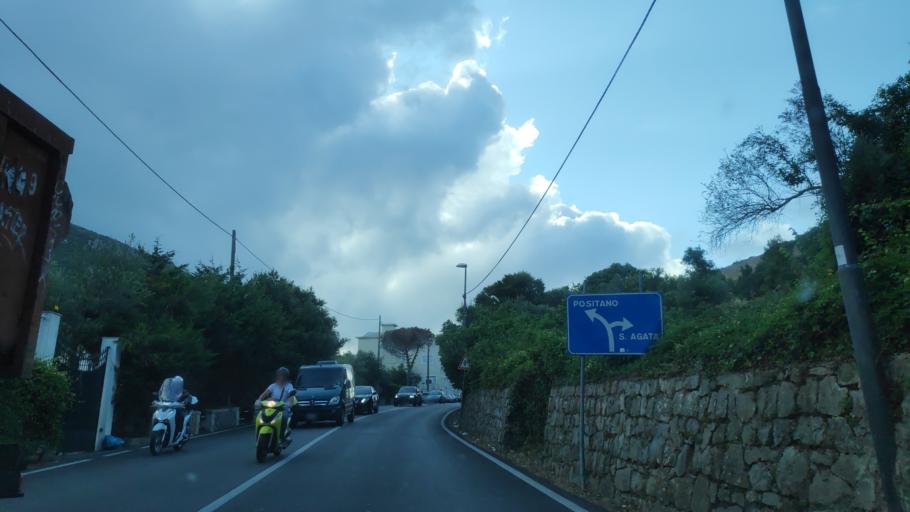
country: IT
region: Campania
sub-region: Provincia di Napoli
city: Piano di Sorrento
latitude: 40.6181
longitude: 14.4255
